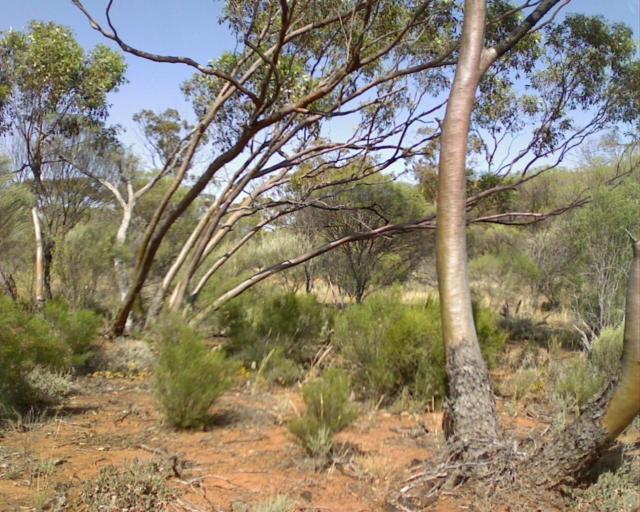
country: AU
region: Western Australia
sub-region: Merredin
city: Merredin
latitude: -30.9543
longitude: 118.8823
